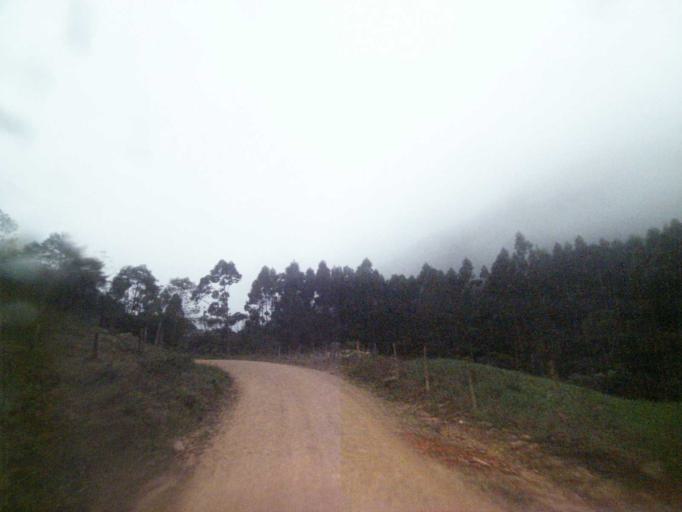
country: BR
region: Santa Catarina
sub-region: Anitapolis
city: Anitapolis
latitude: -27.8066
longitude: -49.1411
